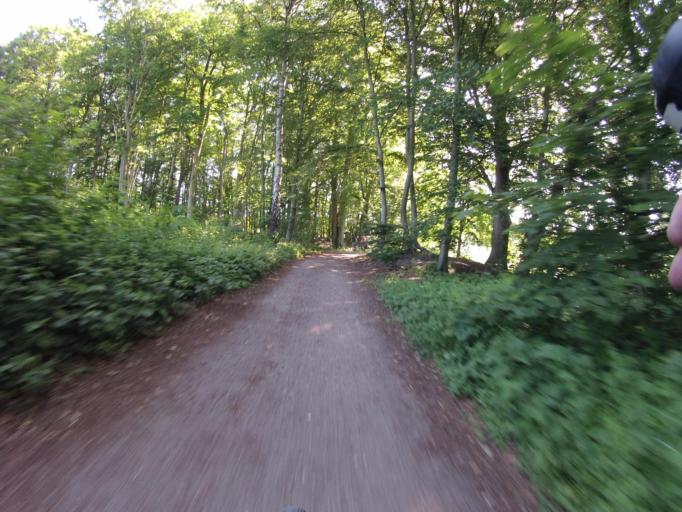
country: DE
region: North Rhine-Westphalia
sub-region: Regierungsbezirk Munster
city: Rheine
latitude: 52.3081
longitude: 7.4115
